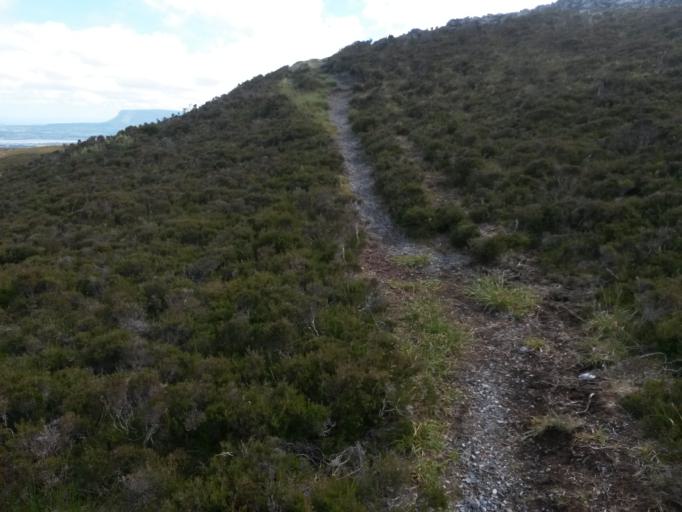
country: IE
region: Connaught
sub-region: Sligo
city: Strandhill
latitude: 54.2606
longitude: -8.5762
